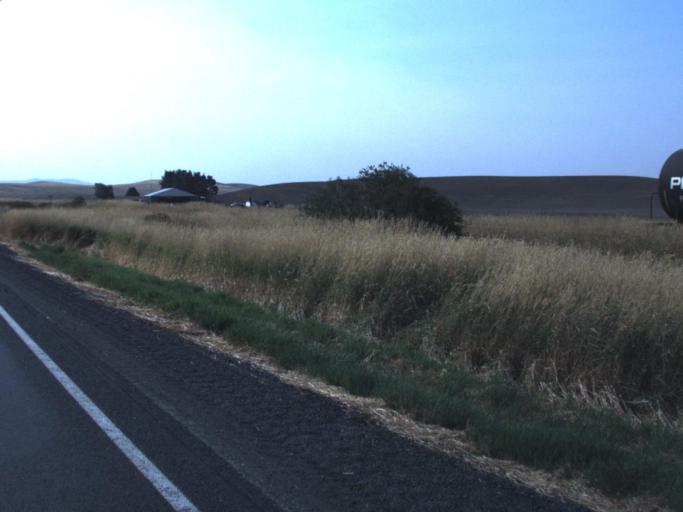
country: US
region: Washington
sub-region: Whitman County
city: Colfax
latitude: 47.0329
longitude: -117.1538
